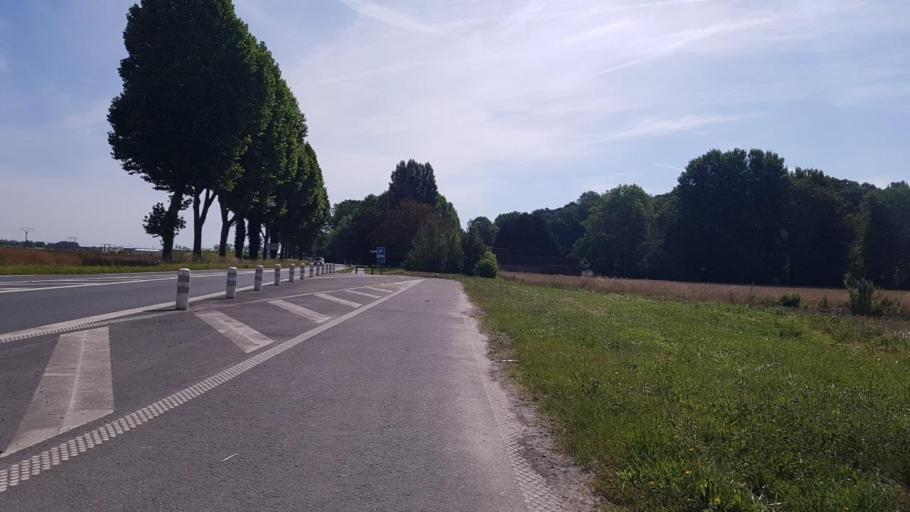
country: FR
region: Picardie
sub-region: Departement de l'Oise
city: Pontpoint
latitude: 49.3085
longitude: 2.6869
